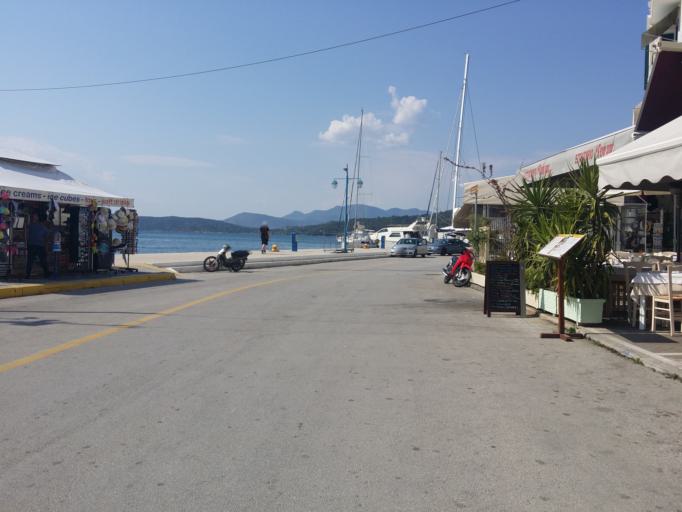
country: GR
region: Attica
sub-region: Nomos Piraios
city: Poros
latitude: 37.4993
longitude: 23.4515
